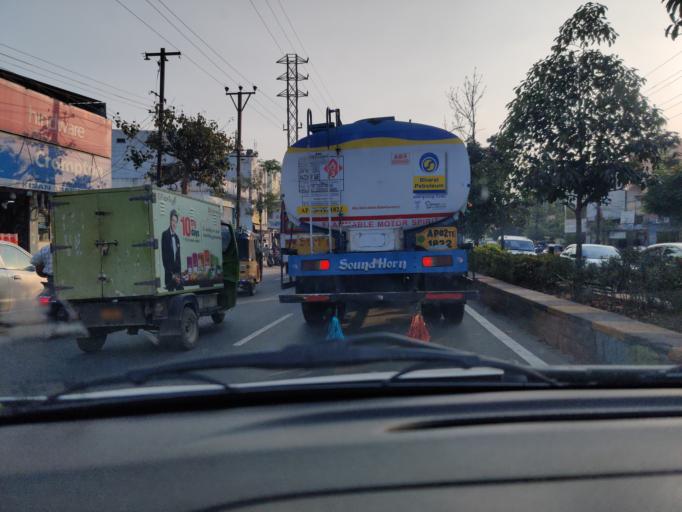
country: IN
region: Telangana
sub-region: Rangareddi
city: Uppal Kalan
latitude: 17.4354
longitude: 78.5545
